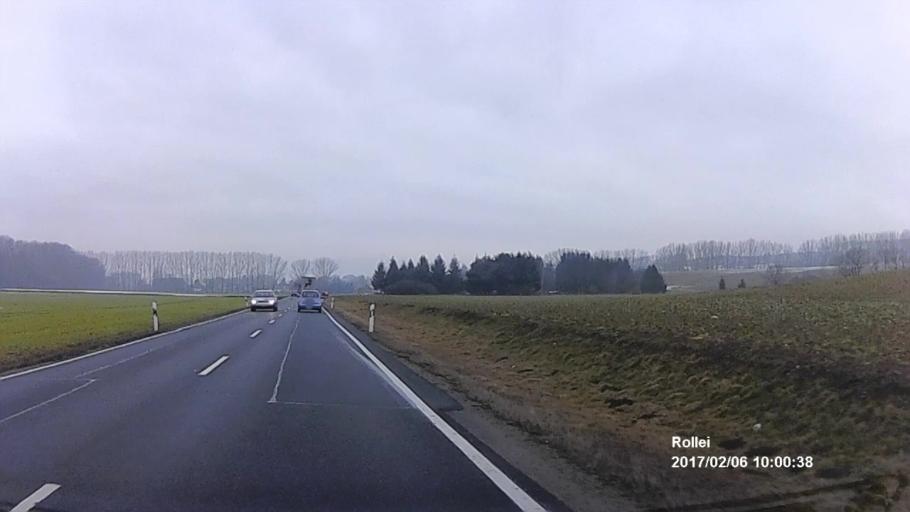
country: DE
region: Thuringia
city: Etzelsrode
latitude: 51.5171
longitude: 10.6774
